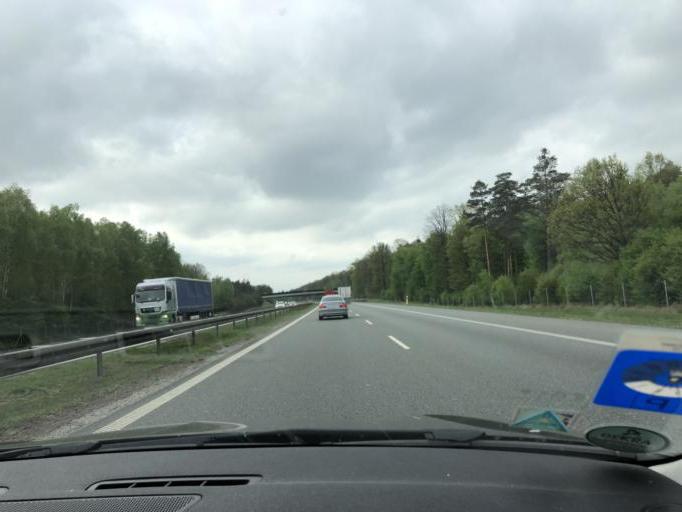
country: PL
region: Opole Voivodeship
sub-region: Powiat opolski
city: Proszkow
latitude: 50.5471
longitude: 17.8946
